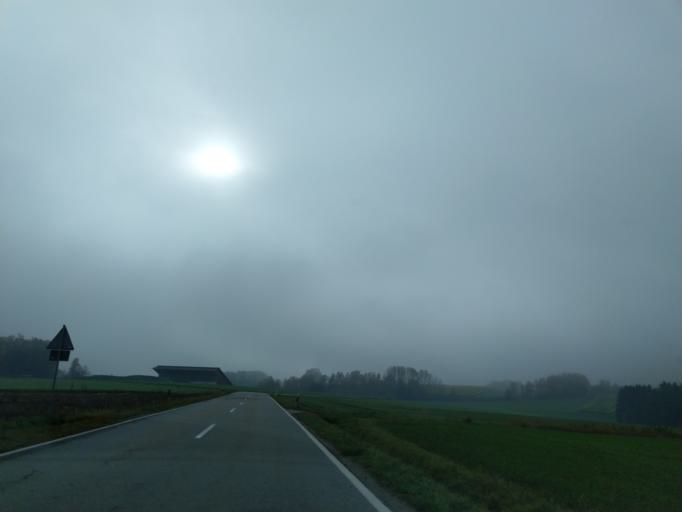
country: DE
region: Bavaria
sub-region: Lower Bavaria
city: Schollnach
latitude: 48.7774
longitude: 13.1701
